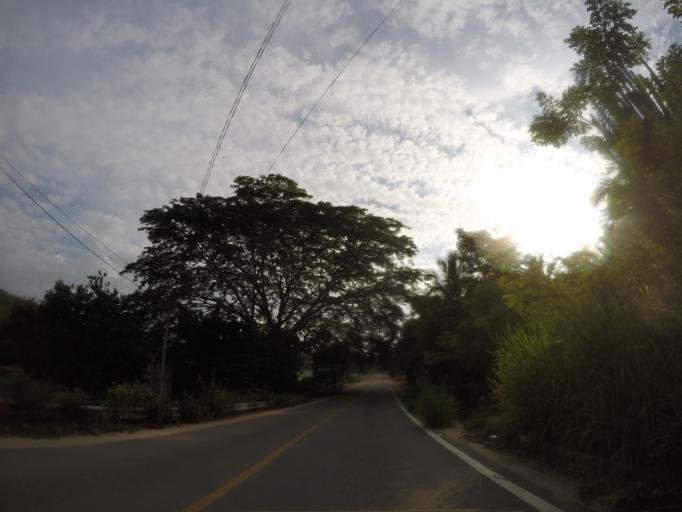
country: MX
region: Oaxaca
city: San Pedro Pochutla
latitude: 15.7124
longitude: -96.4824
